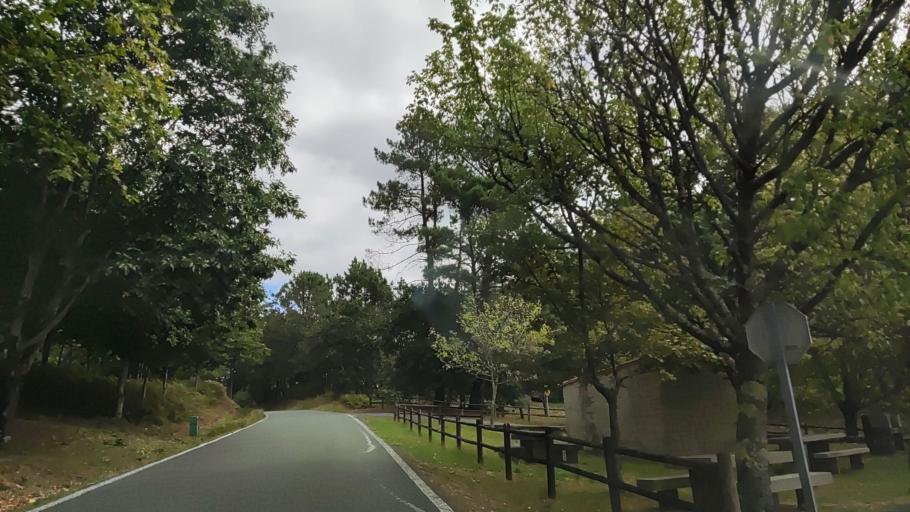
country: ES
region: Galicia
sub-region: Provincia da Coruna
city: Rois
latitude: 42.7328
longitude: -8.7054
